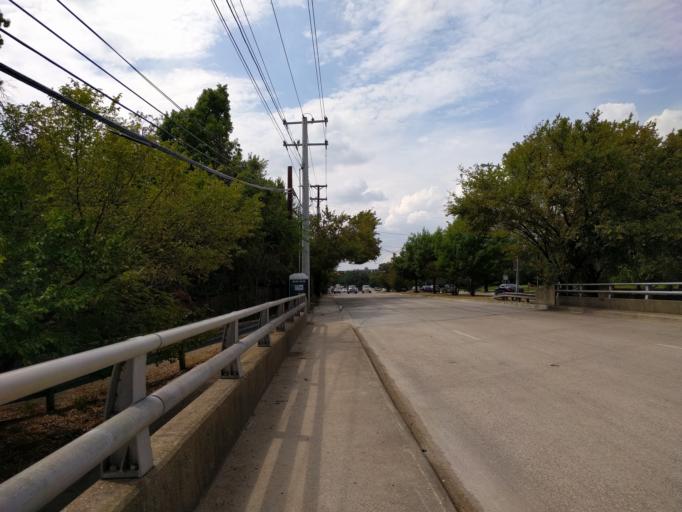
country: US
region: Texas
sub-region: Dallas County
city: Richardson
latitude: 32.9096
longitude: -96.7752
